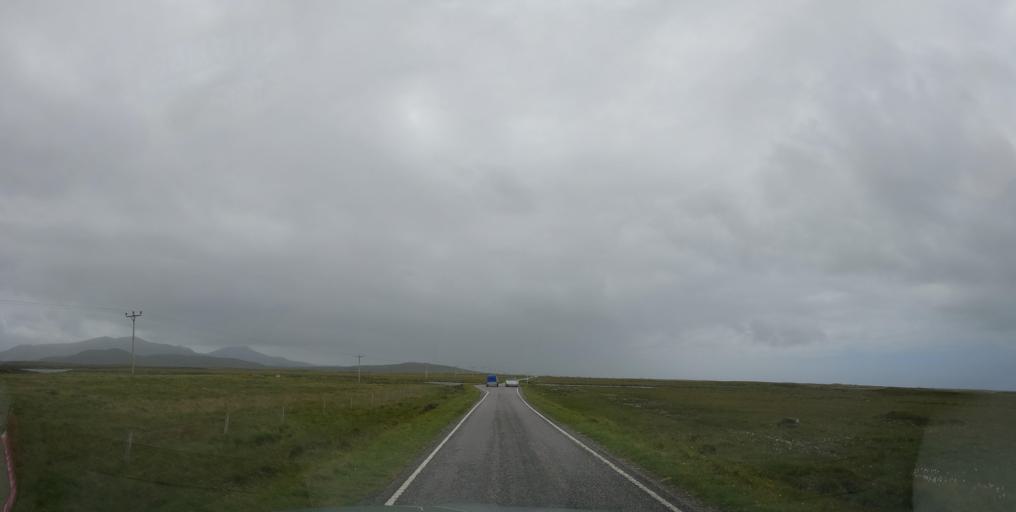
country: GB
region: Scotland
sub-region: Eilean Siar
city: Benbecula
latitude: 57.3735
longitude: -7.3462
